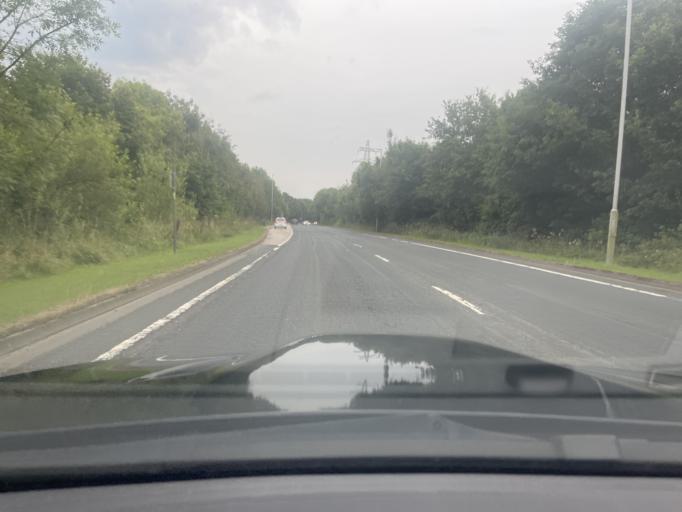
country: GB
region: England
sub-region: Lancashire
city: Leyland
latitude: 53.6950
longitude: -2.7219
